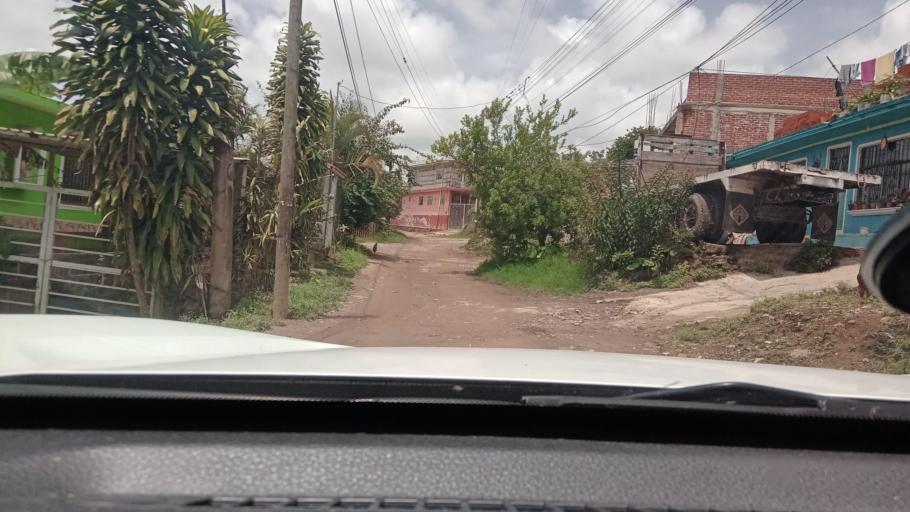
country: MX
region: Veracruz
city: El Castillo
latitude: 19.5488
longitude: -96.8607
